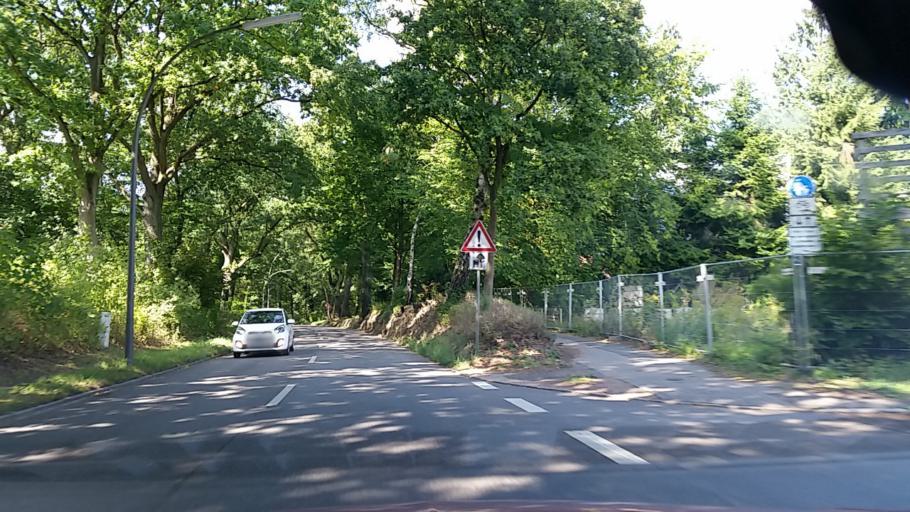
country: DE
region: Hamburg
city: Bergstedt
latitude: 53.6618
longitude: 10.1549
